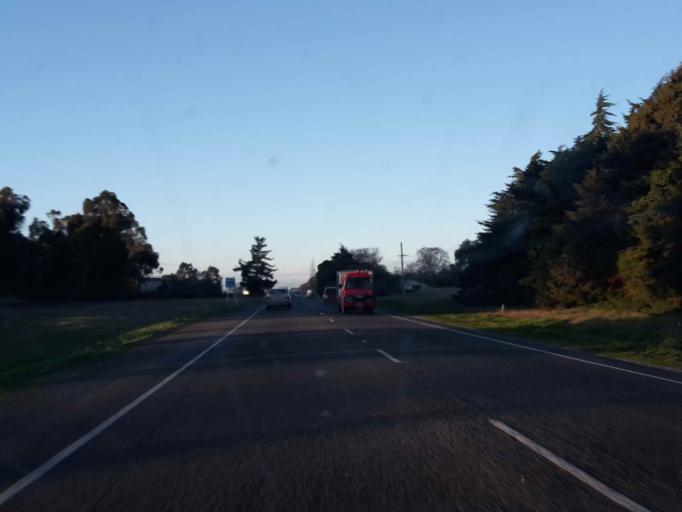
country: NZ
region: Canterbury
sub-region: Selwyn District
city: Rolleston
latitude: -43.5937
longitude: 172.3711
